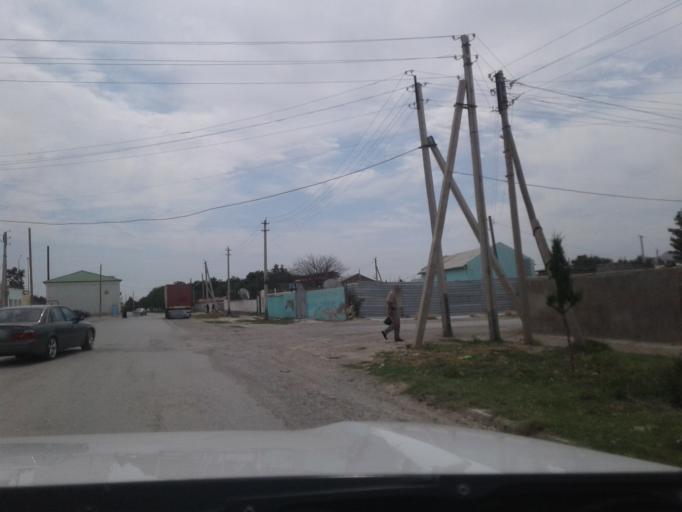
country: TM
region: Balkan
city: Serdar
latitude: 38.9882
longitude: 56.2806
